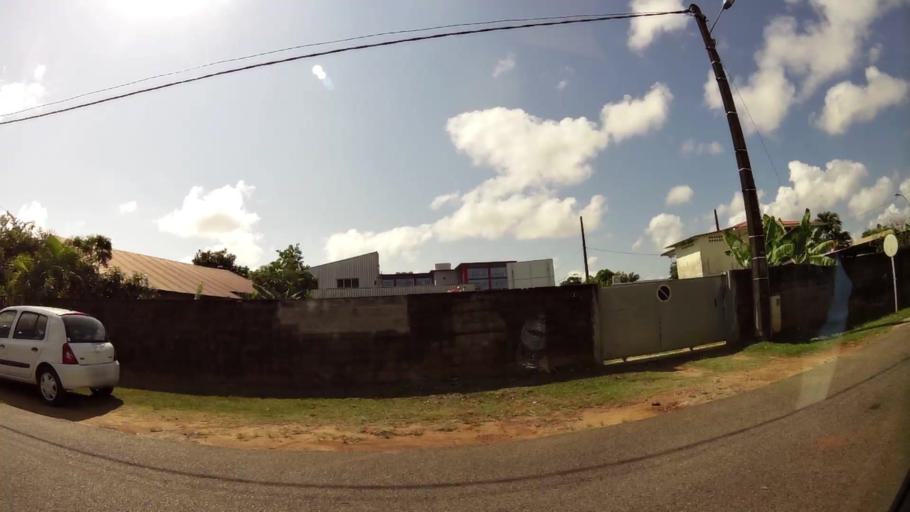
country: GF
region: Guyane
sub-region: Guyane
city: Cayenne
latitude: 4.9366
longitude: -52.3139
